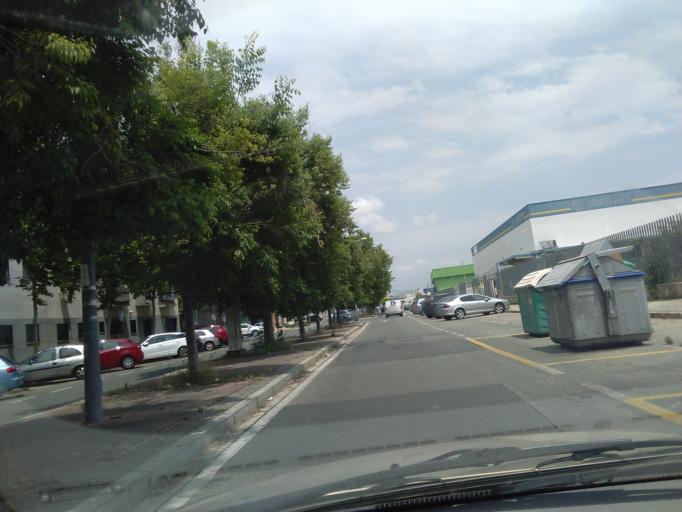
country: ES
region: Andalusia
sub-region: Provincia de Sevilla
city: Sevilla
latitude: 37.3800
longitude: -5.9403
